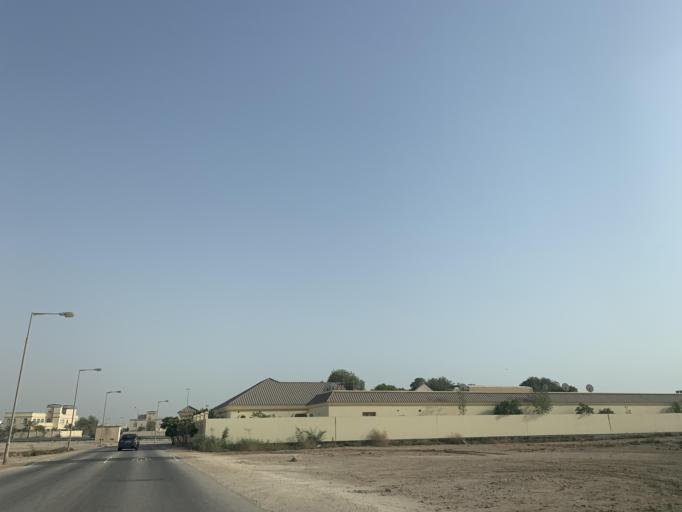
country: BH
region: Central Governorate
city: Madinat Hamad
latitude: 26.1749
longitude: 50.4741
